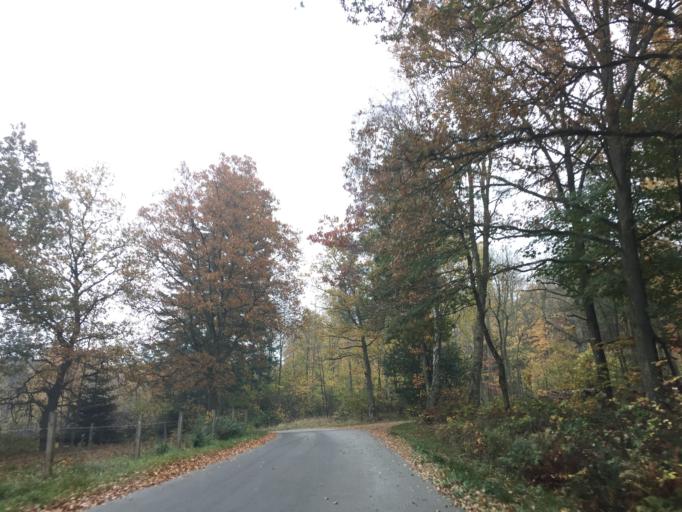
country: SE
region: Skane
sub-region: Lunds Kommun
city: Veberod
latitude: 55.6149
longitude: 13.5017
